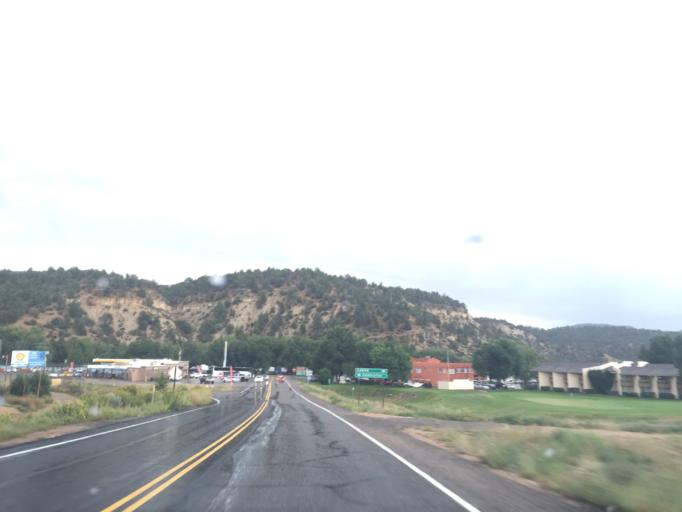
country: US
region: Utah
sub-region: Kane County
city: Kanab
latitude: 37.2247
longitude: -112.6831
